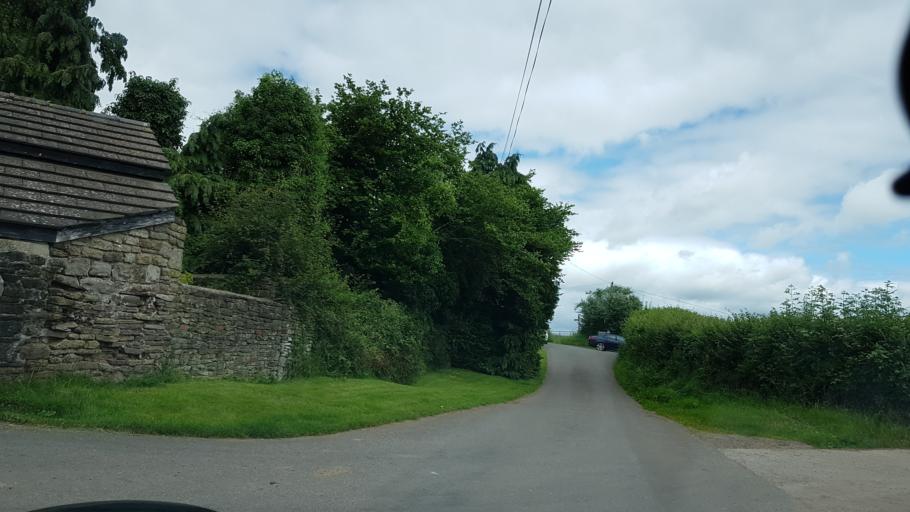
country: GB
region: Wales
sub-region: Monmouthshire
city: Llanarth
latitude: 51.8453
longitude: -2.9006
